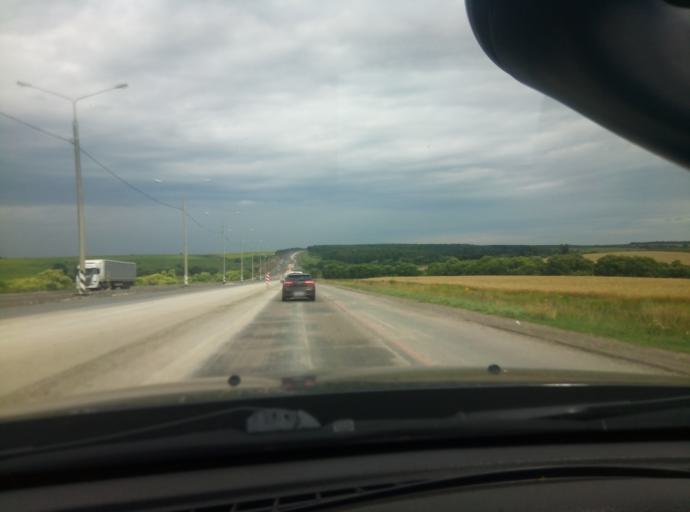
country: RU
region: Tula
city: Novogurovskiy
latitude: 54.4888
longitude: 37.5126
